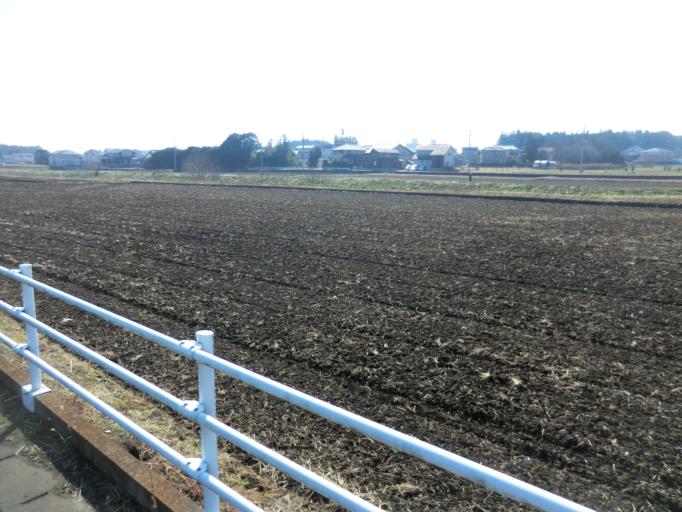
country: JP
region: Ibaraki
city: Naka
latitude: 36.0731
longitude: 140.1411
